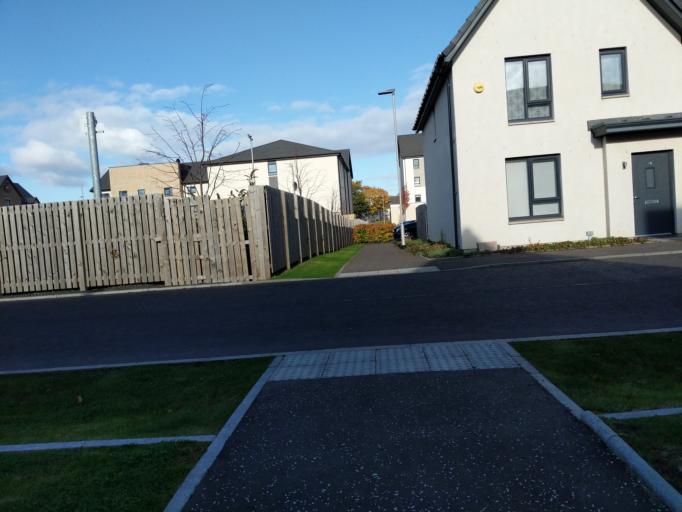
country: GB
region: Scotland
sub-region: Edinburgh
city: Currie
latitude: 55.9327
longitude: -3.3023
